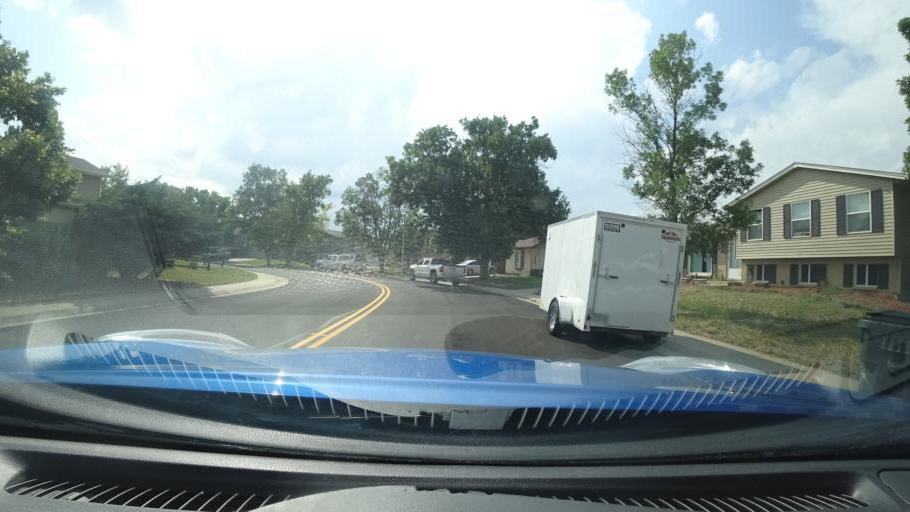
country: US
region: Colorado
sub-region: Adams County
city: Aurora
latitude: 39.6877
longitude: -104.7858
